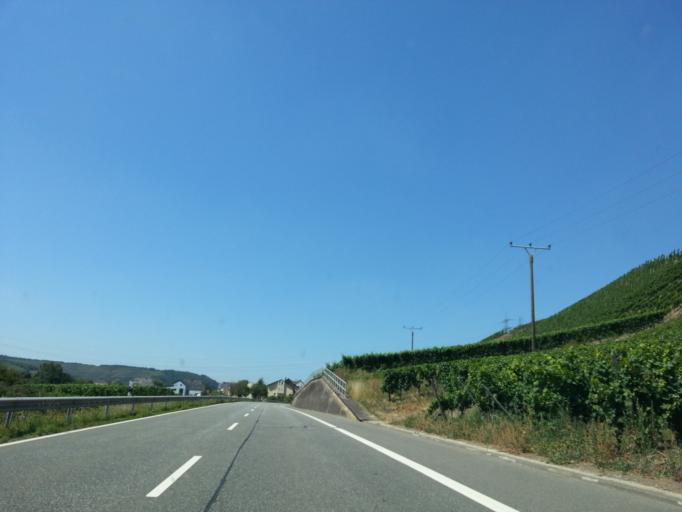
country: DE
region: Rheinland-Pfalz
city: Longuich
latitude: 49.8025
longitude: 6.7945
